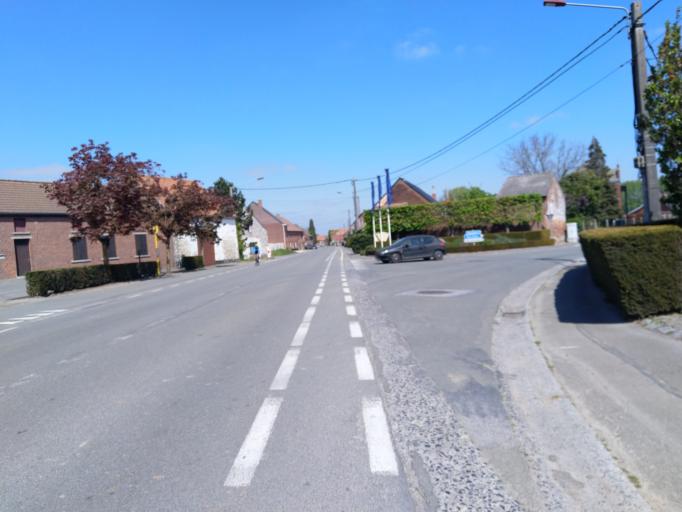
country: BE
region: Wallonia
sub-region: Province du Hainaut
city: Chievres
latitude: 50.5296
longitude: 3.7938
